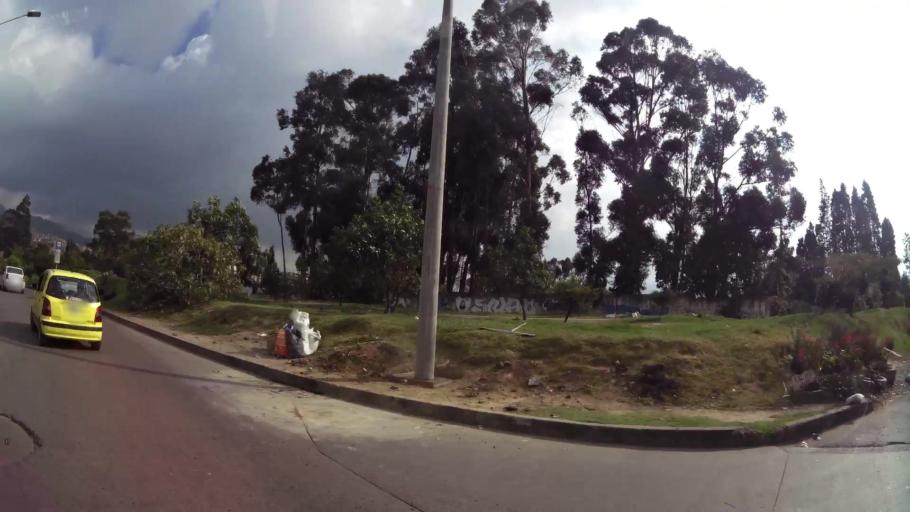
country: CO
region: Bogota D.C.
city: Bogota
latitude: 4.5531
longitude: -74.1193
